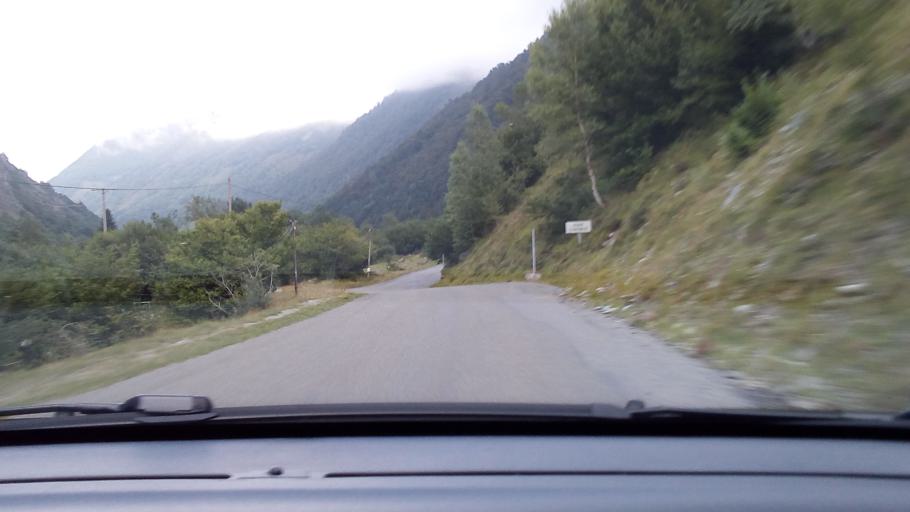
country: FR
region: Midi-Pyrenees
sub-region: Departement des Hautes-Pyrenees
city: Cauterets
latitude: 42.9111
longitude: -0.1972
